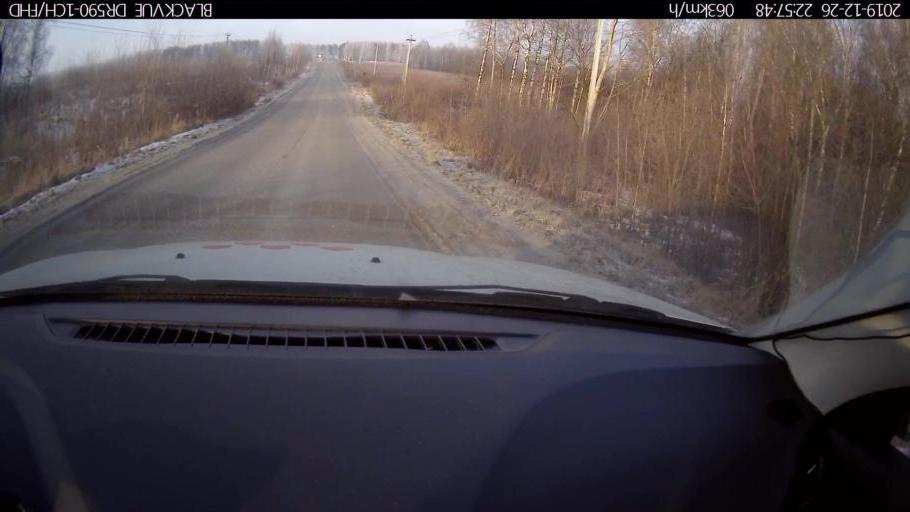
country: RU
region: Nizjnij Novgorod
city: Burevestnik
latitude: 56.1535
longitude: 43.7123
